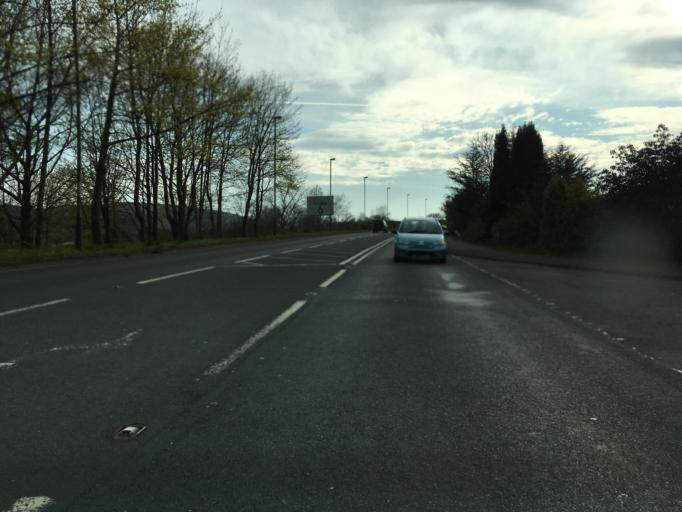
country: GB
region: Wales
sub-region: Caerphilly County Borough
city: Caerphilly
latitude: 51.5728
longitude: -3.2377
